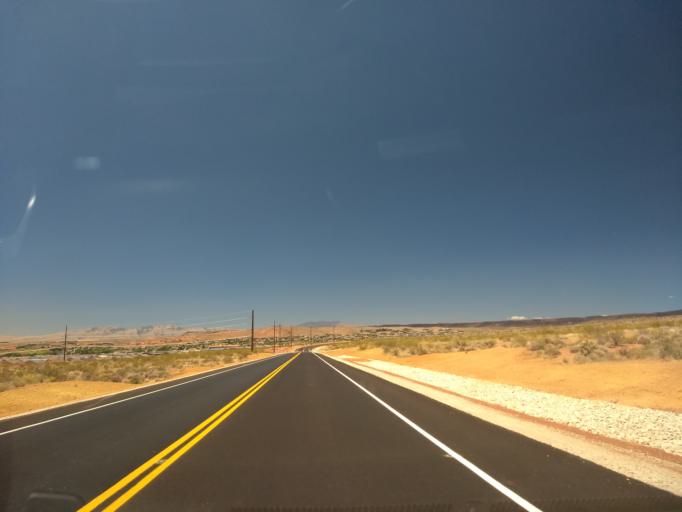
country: US
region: Utah
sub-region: Washington County
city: Washington
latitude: 37.1484
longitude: -113.5071
